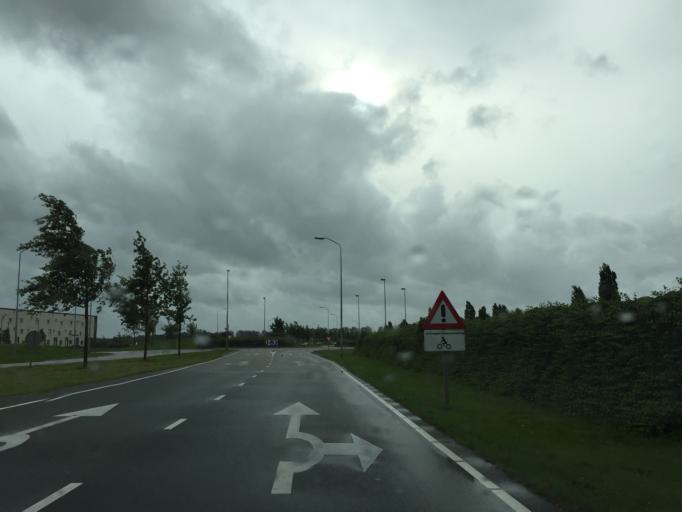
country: NL
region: Flevoland
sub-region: Gemeente Lelystad
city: Lelystad
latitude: 52.4924
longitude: 5.4524
